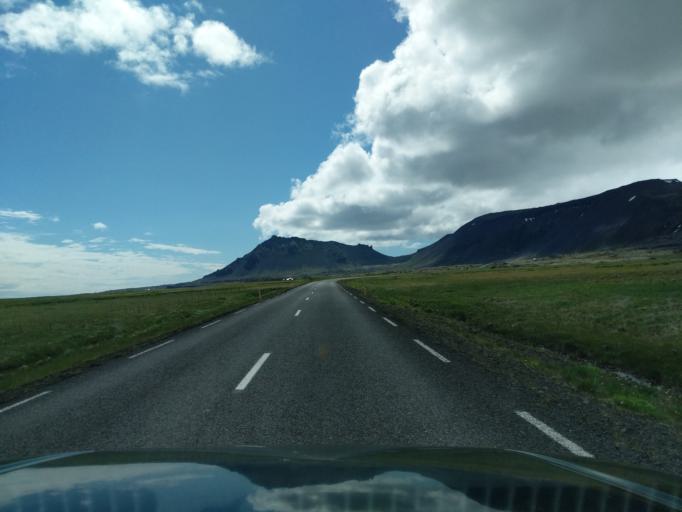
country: IS
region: West
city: Olafsvik
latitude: 64.8126
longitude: -23.5864
